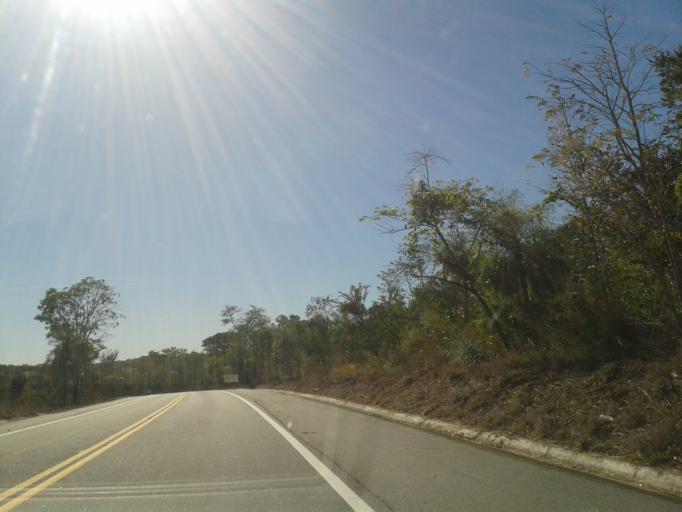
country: BR
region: Goias
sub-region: Goias
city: Goias
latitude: -15.7539
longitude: -50.1644
